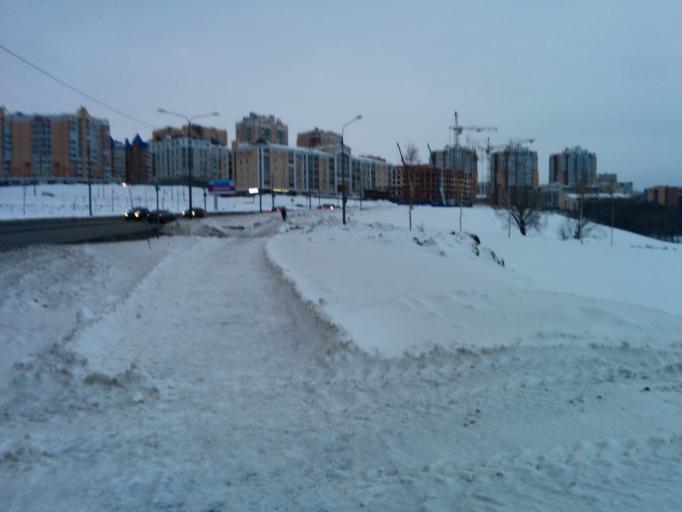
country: RU
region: Chuvashia
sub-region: Cheboksarskiy Rayon
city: Cheboksary
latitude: 56.1382
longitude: 47.2327
